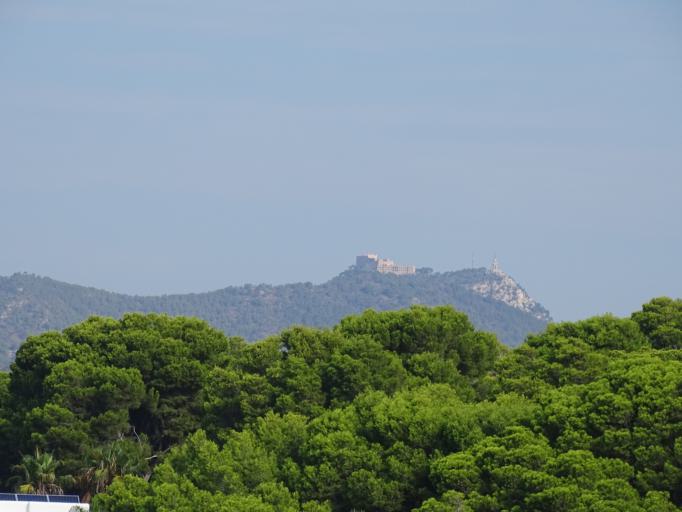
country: ES
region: Balearic Islands
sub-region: Illes Balears
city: Santanyi
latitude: 39.3669
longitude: 3.2339
